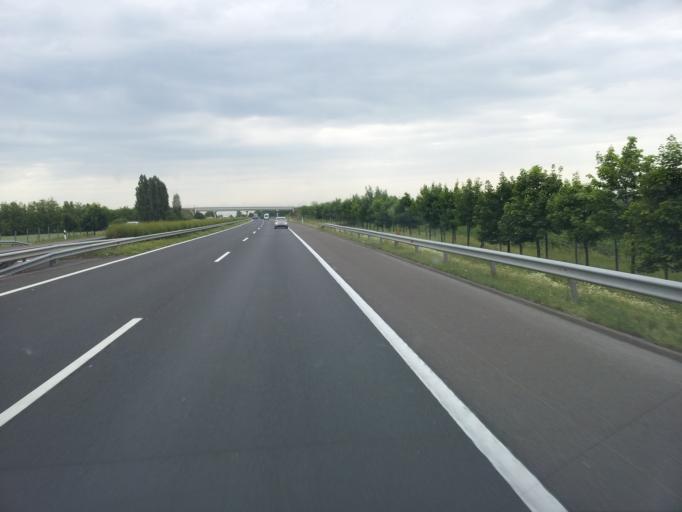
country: HU
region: Heves
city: Karacsond
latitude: 47.7040
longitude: 20.0586
